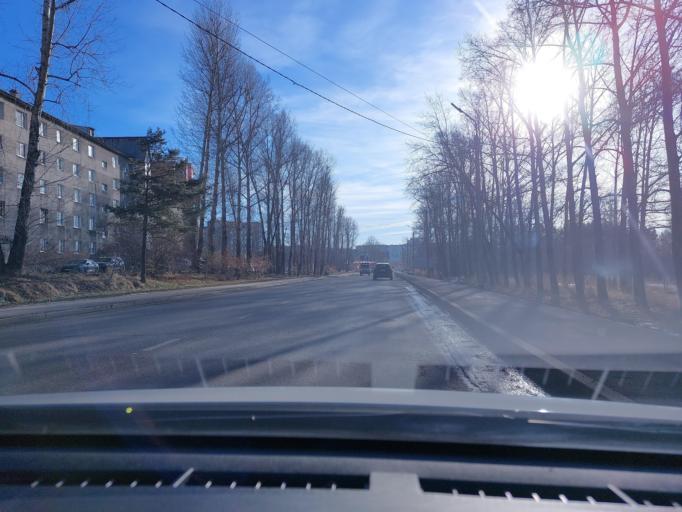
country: RU
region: Irkutsk
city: Dzerzhinsk
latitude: 52.2556
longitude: 104.3521
